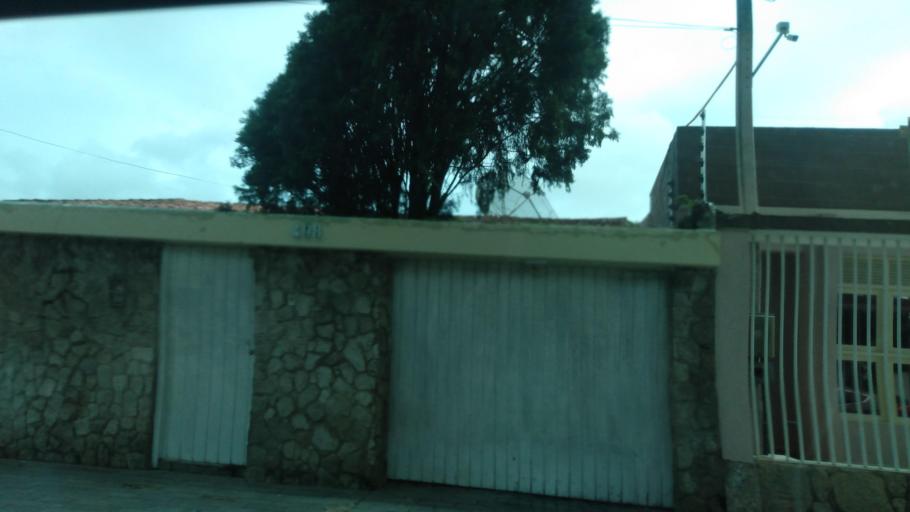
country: BR
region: Pernambuco
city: Garanhuns
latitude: -8.8832
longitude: -36.4779
